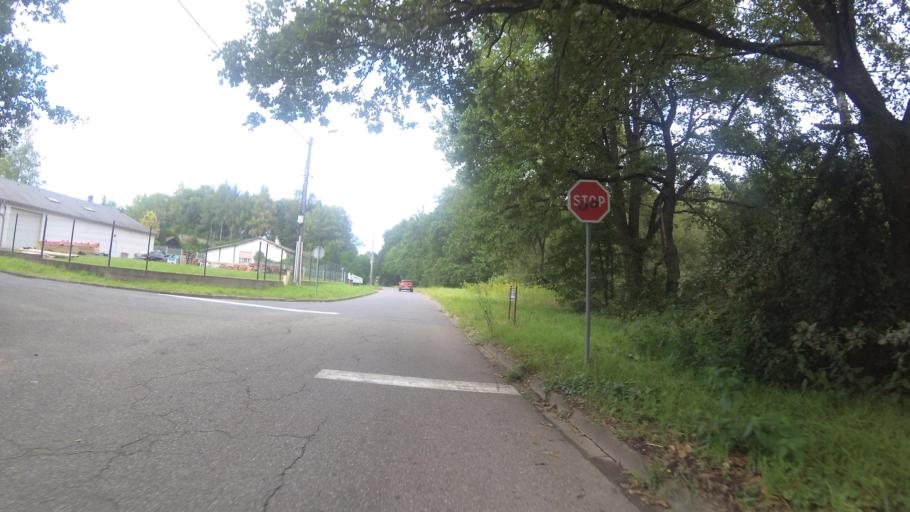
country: FR
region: Lorraine
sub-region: Departement de la Moselle
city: Carling
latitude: 49.1995
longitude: 6.7154
